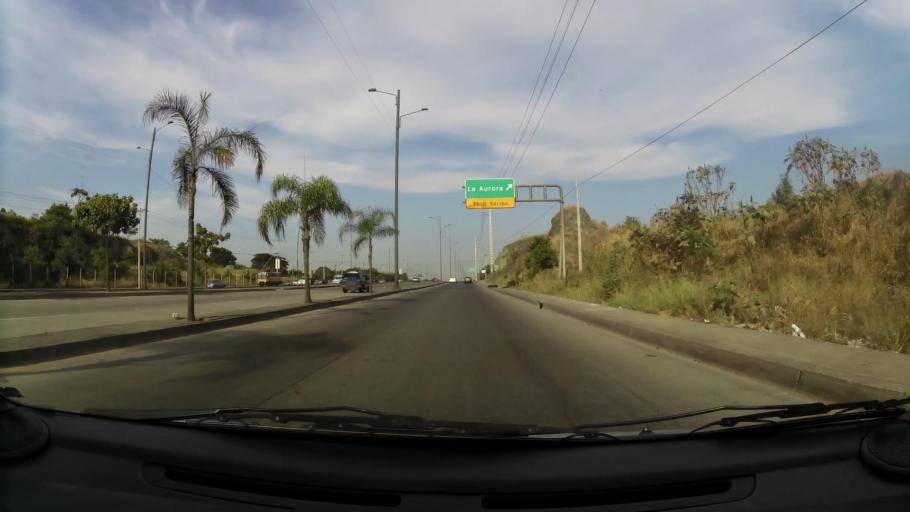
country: EC
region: Guayas
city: Eloy Alfaro
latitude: -2.0713
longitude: -79.9163
